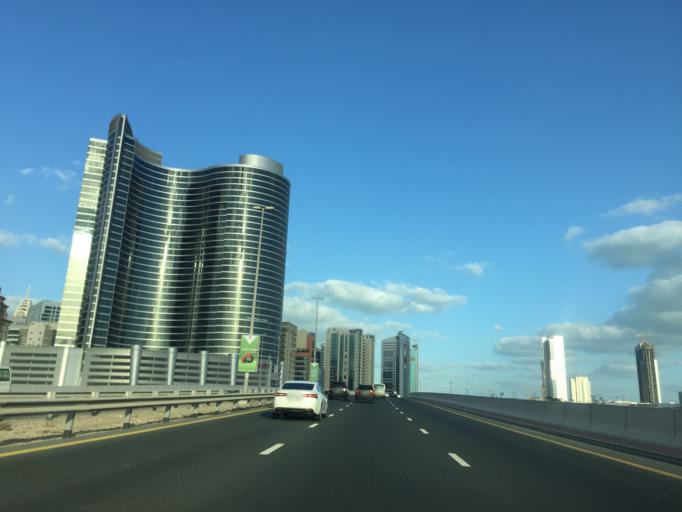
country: AE
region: Dubai
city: Dubai
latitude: 25.0952
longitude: 55.1835
